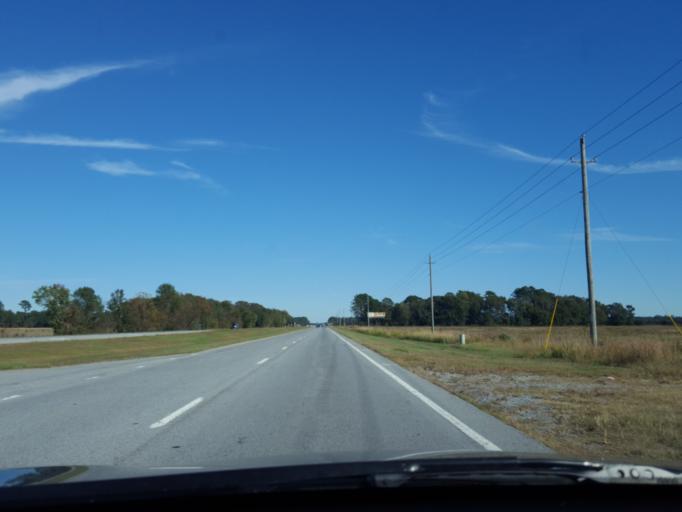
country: US
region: North Carolina
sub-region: Pitt County
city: Greenville
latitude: 35.6257
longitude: -77.3066
